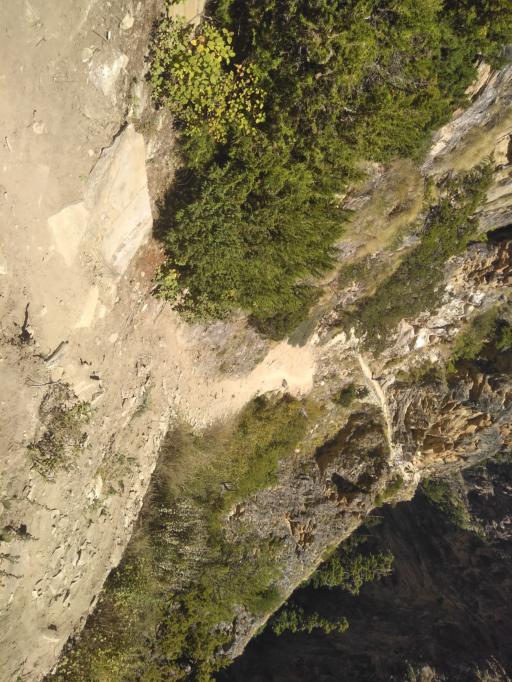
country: NP
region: Western Region
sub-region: Dhawalagiri Zone
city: Jomsom
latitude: 28.9528
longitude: 83.0693
